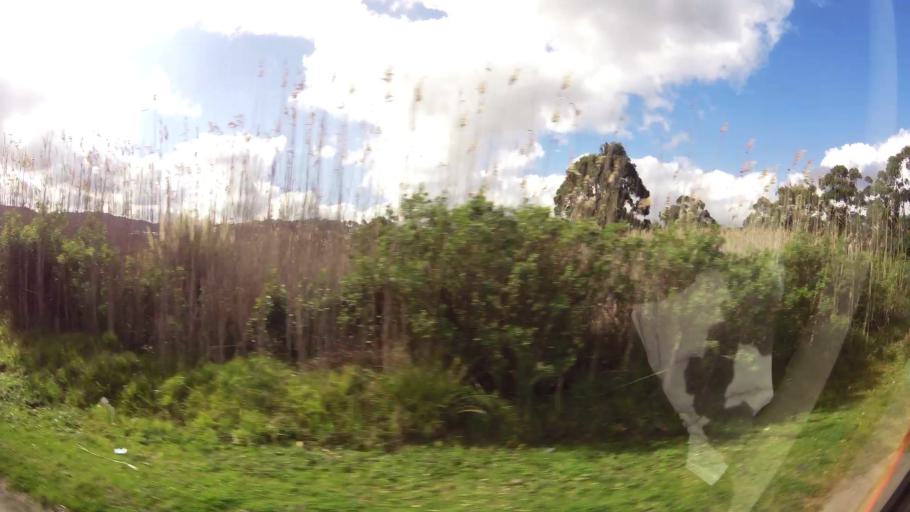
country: ZA
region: Western Cape
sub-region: Eden District Municipality
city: Knysna
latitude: -34.0530
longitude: 23.0699
